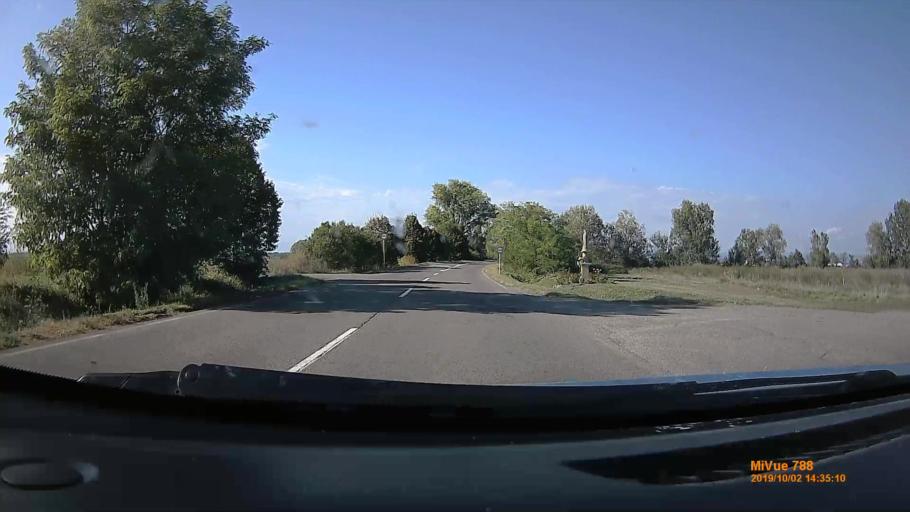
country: HU
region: Borsod-Abauj-Zemplen
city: Mezokovesd
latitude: 47.7813
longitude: 20.5825
